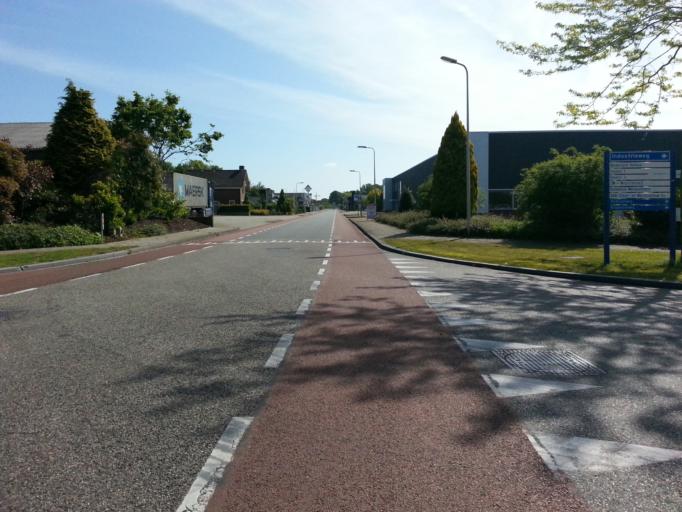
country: NL
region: Gelderland
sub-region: Berkelland
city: Neede
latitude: 52.1301
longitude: 6.6266
